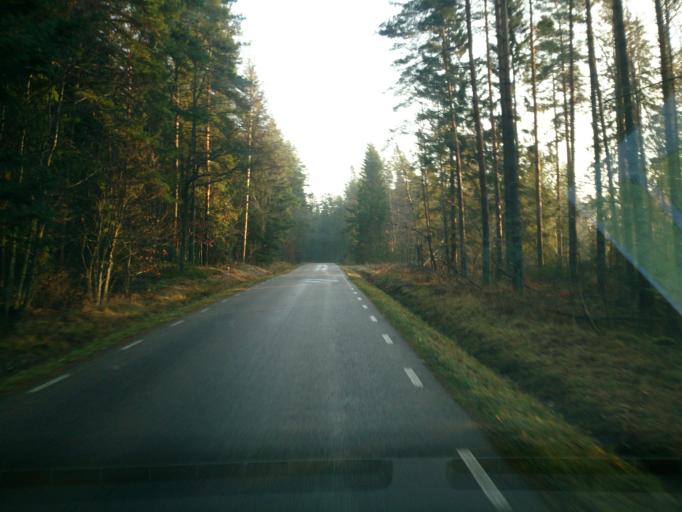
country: SE
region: OEstergoetland
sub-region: Atvidabergs Kommun
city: Atvidaberg
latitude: 58.3323
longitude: 15.9825
